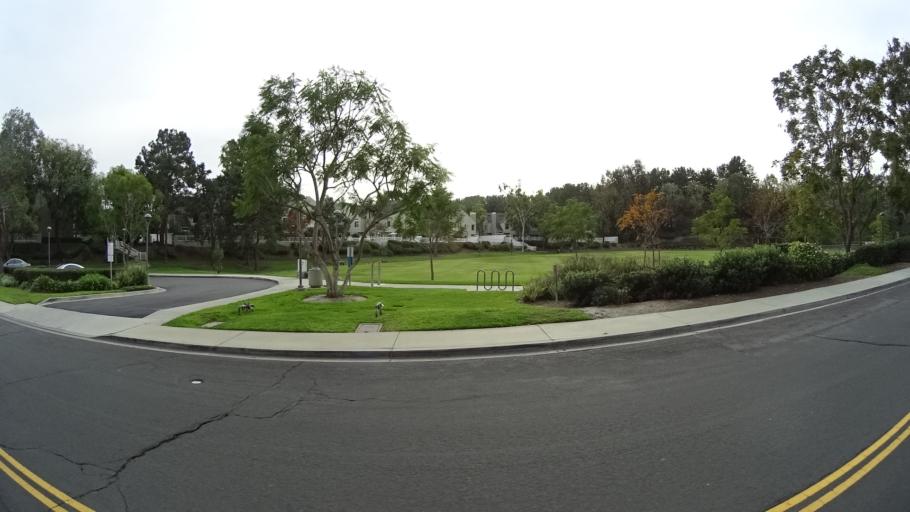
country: US
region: California
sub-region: Orange County
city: Laguna Woods
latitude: 33.5932
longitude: -117.7213
